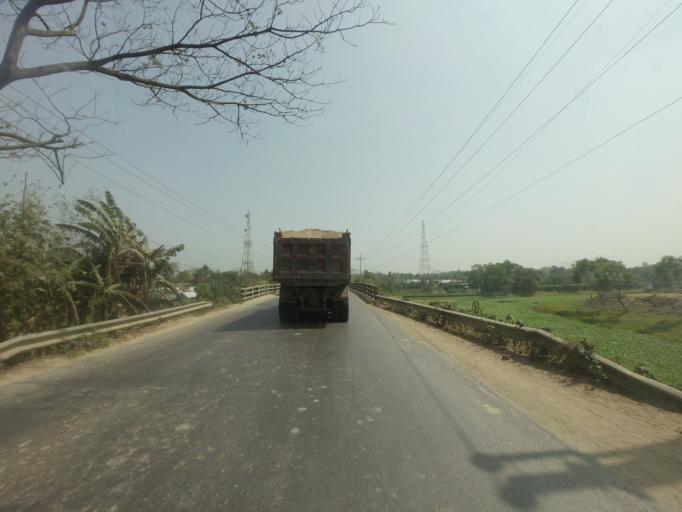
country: BD
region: Dhaka
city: Bhairab Bazar
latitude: 24.0523
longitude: 91.1658
